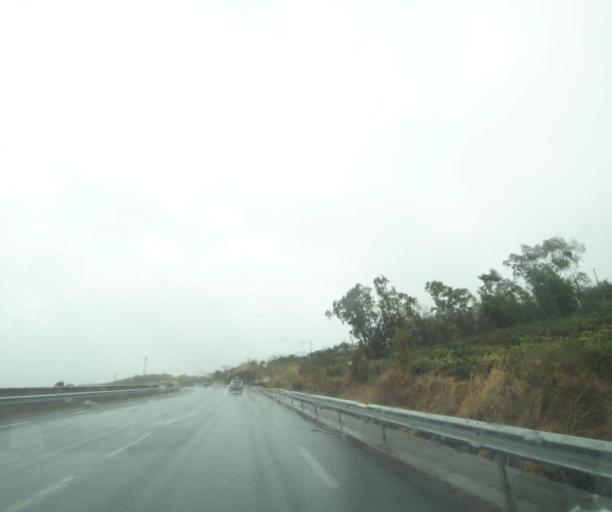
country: RE
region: Reunion
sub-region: Reunion
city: Le Port
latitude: -20.9726
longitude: 55.3146
